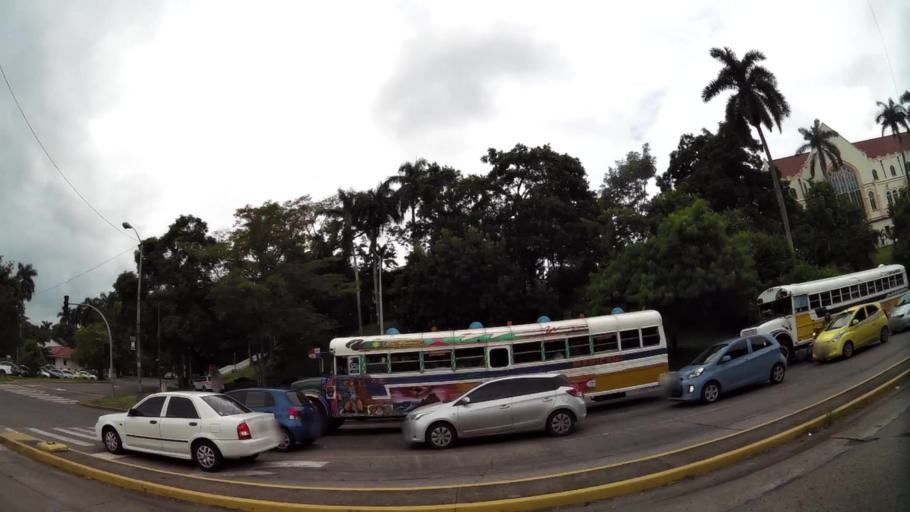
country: PA
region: Panama
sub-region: Distrito de Panama
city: Ancon
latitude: 8.9530
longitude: -79.5566
